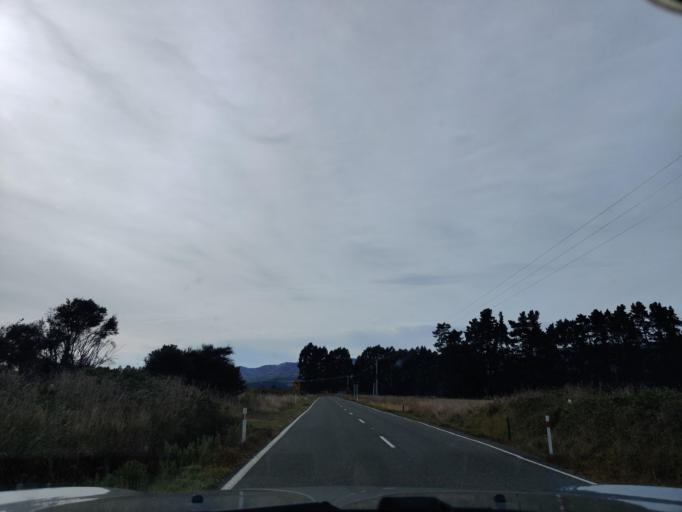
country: NZ
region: Tasman
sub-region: Tasman District
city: Brightwater
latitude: -41.6572
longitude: 173.2339
